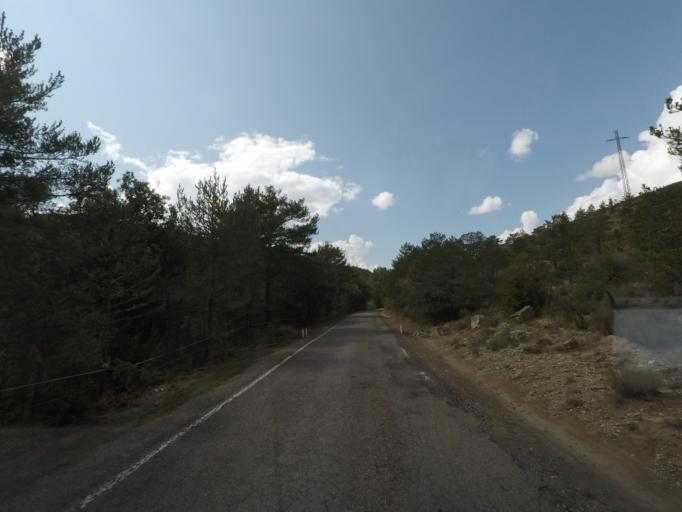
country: ES
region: Aragon
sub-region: Provincia de Huesca
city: Fiscal
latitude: 42.4078
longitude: -0.1954
